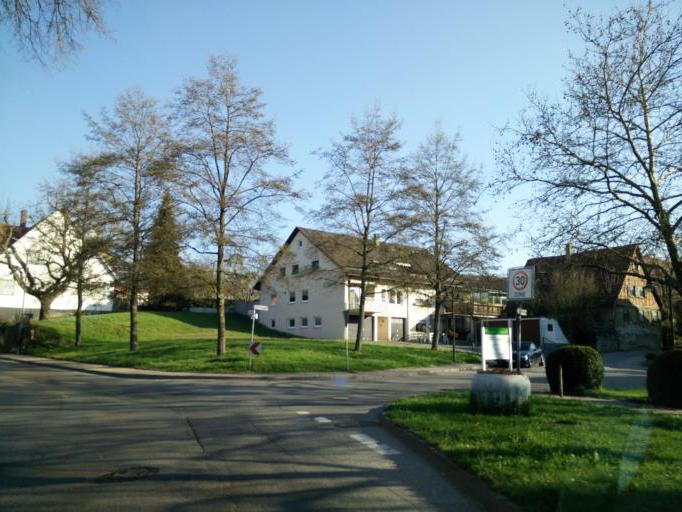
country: DE
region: Baden-Wuerttemberg
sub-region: Regierungsbezirk Stuttgart
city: Deckenpfronn
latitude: 48.6241
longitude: 8.8348
